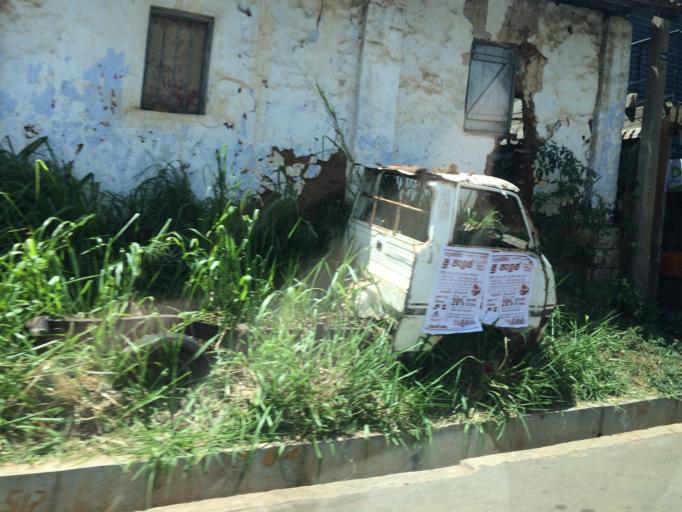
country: LK
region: Central
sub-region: Nuwara Eliya District
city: Nuwara Eliya
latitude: 6.9056
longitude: 80.8487
